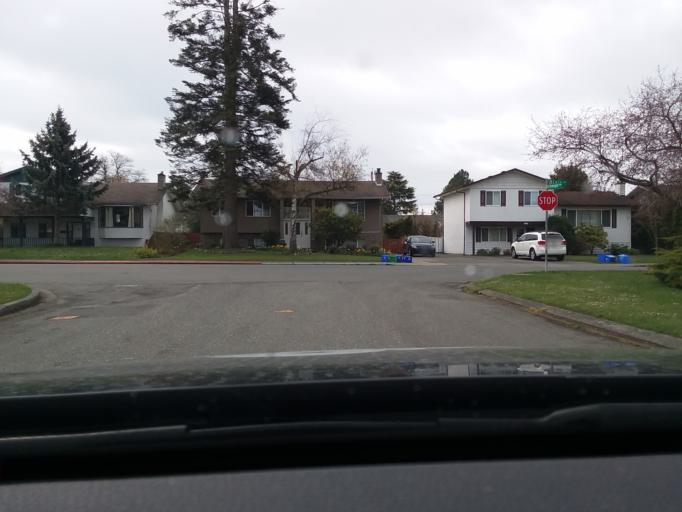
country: CA
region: British Columbia
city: Oak Bay
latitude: 48.4731
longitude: -123.3266
